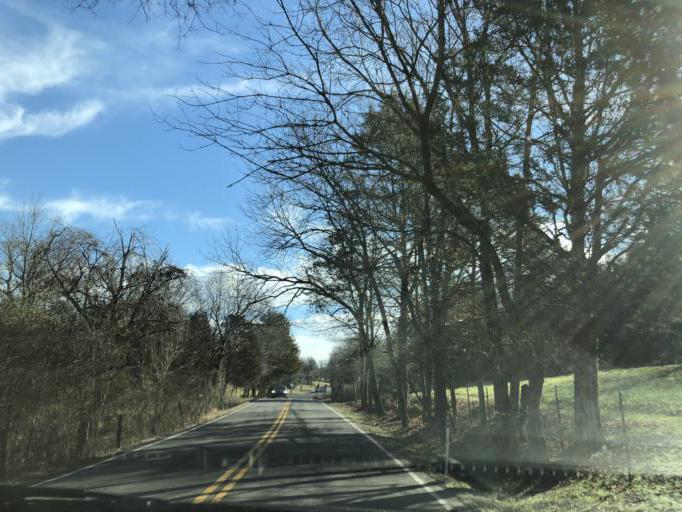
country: US
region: Tennessee
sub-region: Wilson County
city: Green Hill
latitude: 36.1719
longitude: -86.5652
